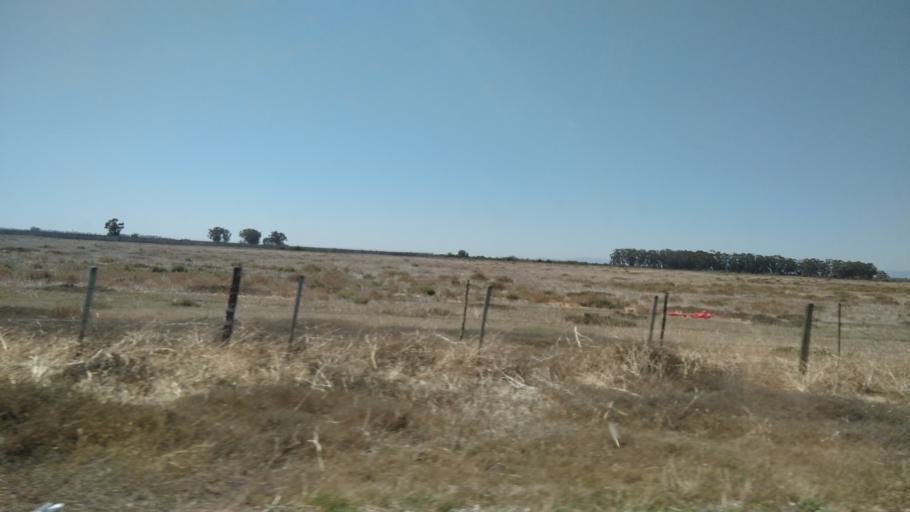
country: ZA
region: Western Cape
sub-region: West Coast District Municipality
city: Vredenburg
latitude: -32.9911
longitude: 18.1662
